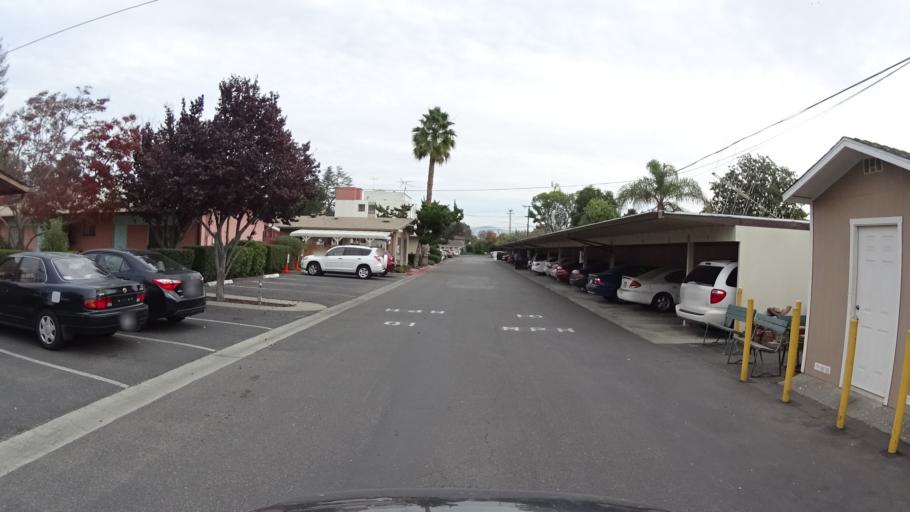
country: US
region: California
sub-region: Santa Clara County
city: Burbank
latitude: 37.3316
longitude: -121.9523
